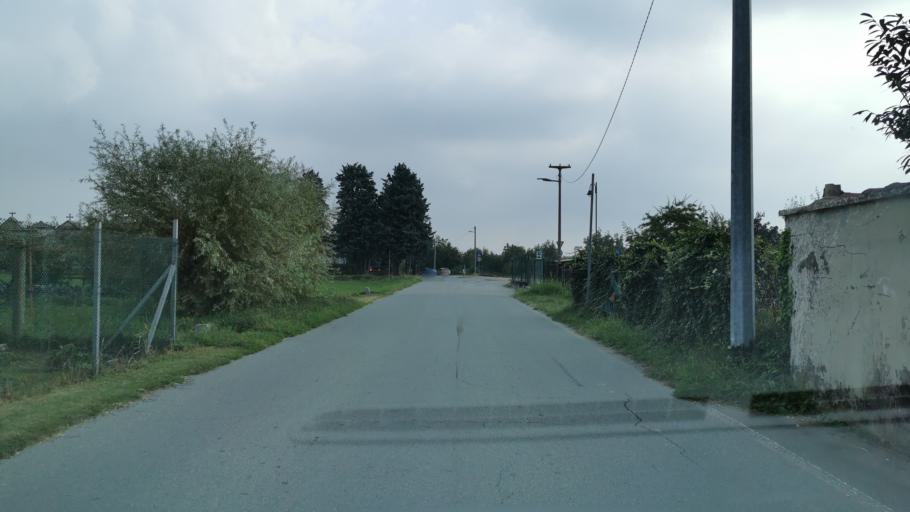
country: IT
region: Piedmont
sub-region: Provincia di Torino
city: Tonengo-Casale
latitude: 45.2891
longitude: 7.9397
